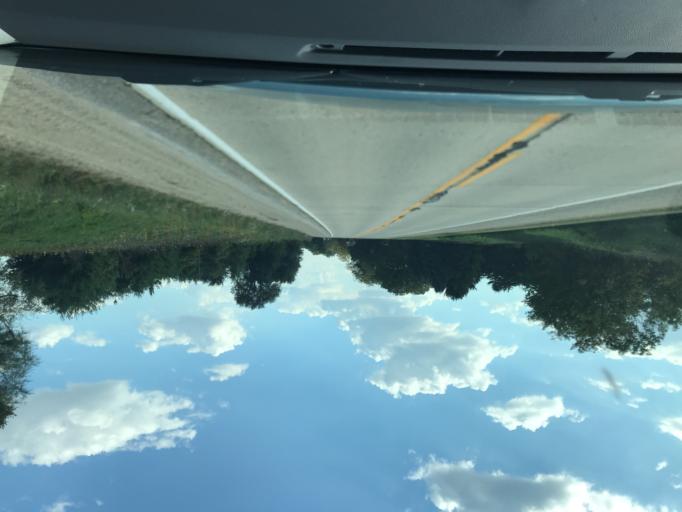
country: US
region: Wisconsin
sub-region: Rock County
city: Orfordville
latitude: 42.5301
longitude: -89.2355
